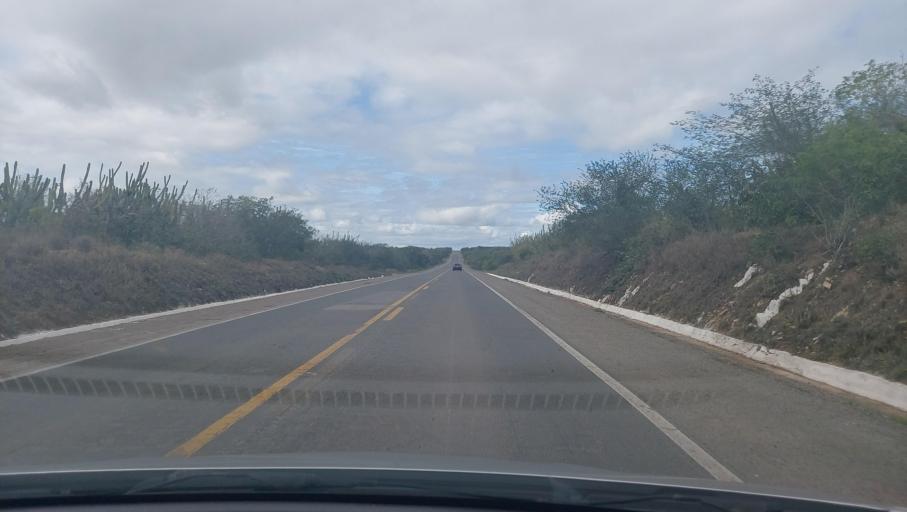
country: BR
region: Bahia
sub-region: Ipira
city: Ipira
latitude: -12.4938
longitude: -39.8221
